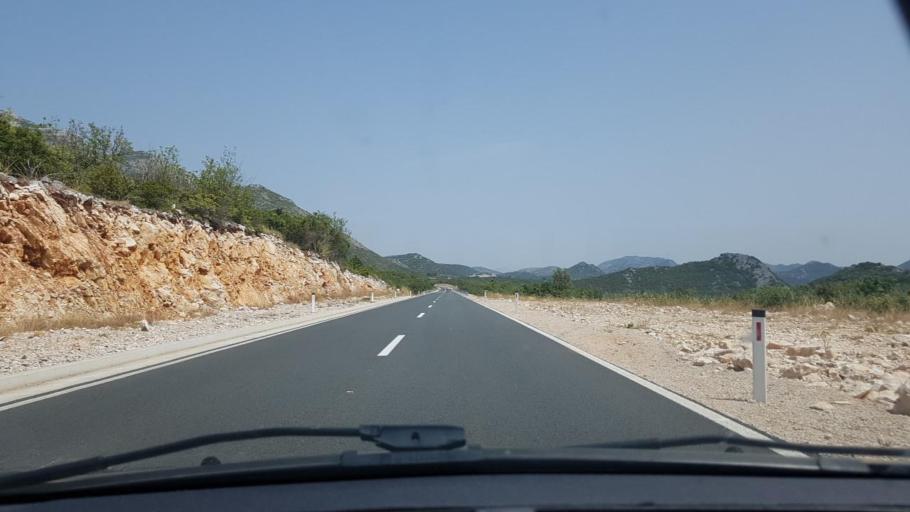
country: BA
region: Federation of Bosnia and Herzegovina
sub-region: Hercegovacko-Bosanski Kanton
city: Neum
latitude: 42.9602
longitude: 17.7076
